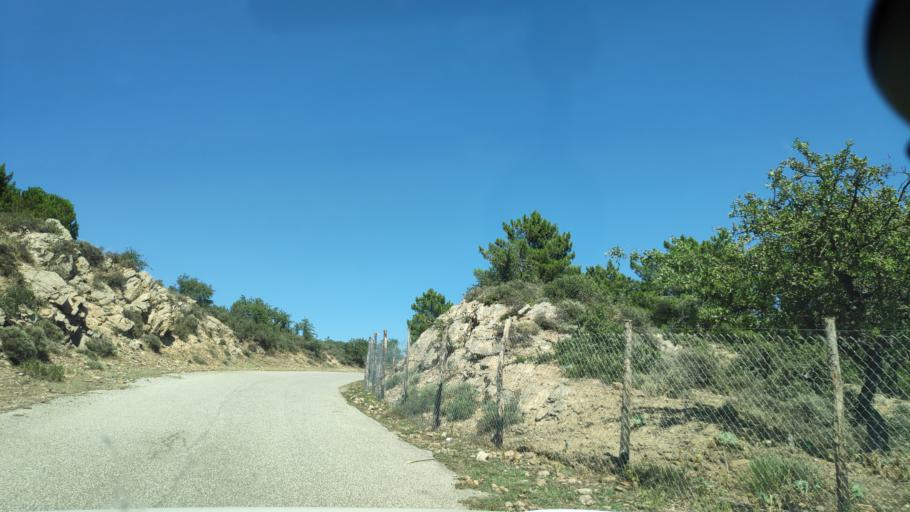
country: IT
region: Calabria
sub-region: Provincia di Reggio Calabria
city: Bova
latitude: 38.0215
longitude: 15.9377
